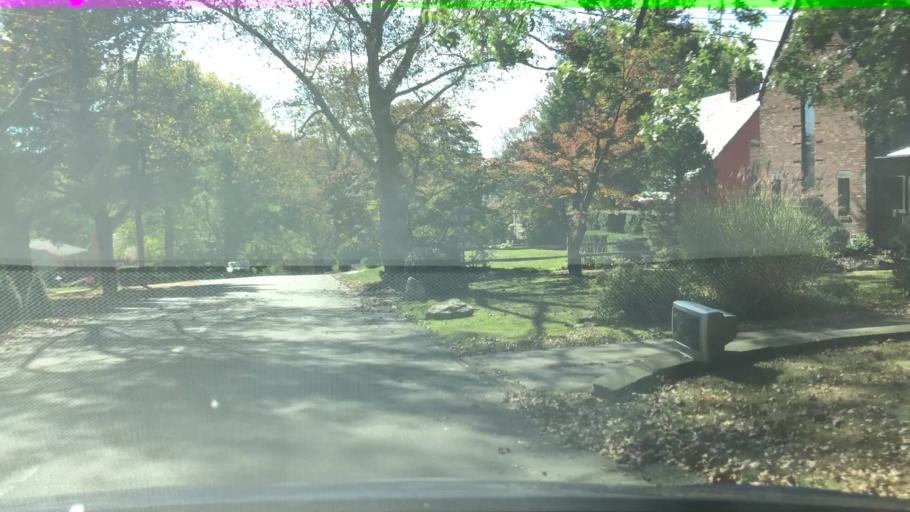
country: US
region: Pennsylvania
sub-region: Allegheny County
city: Penn Hills
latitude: 40.4728
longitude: -79.8274
